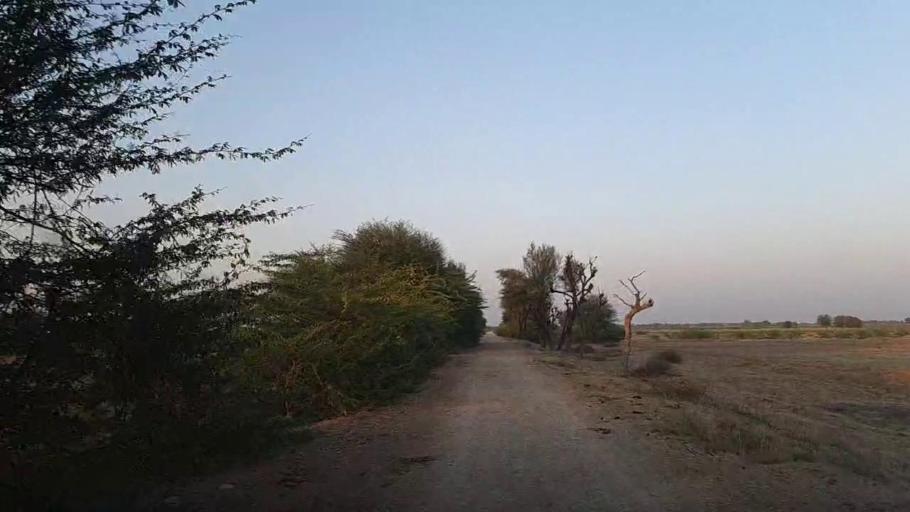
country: PK
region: Sindh
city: Naukot
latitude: 24.8724
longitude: 69.3484
